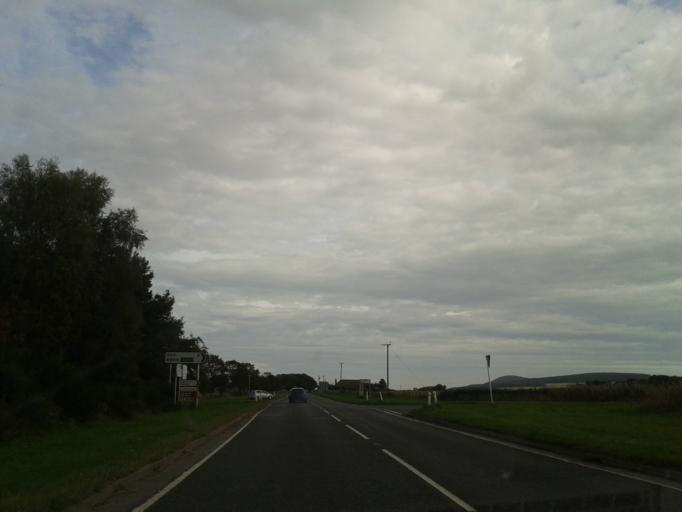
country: GB
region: Scotland
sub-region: Moray
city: Buckie
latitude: 57.6466
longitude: -3.0166
